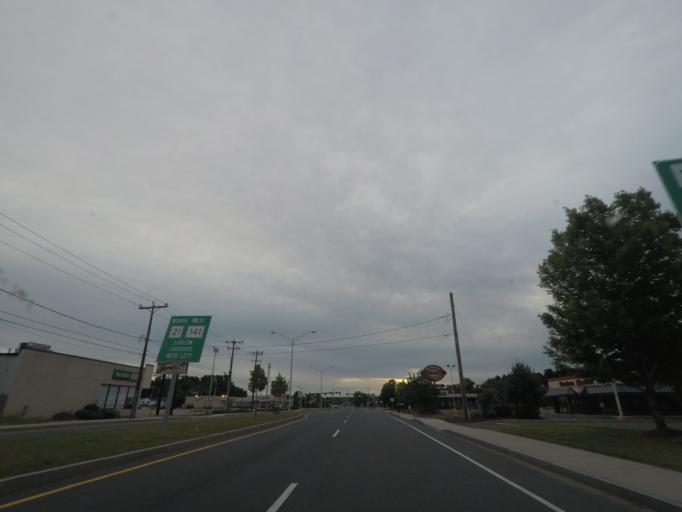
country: US
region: Massachusetts
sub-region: Hampden County
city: Ludlow
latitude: 42.1409
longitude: -72.4980
